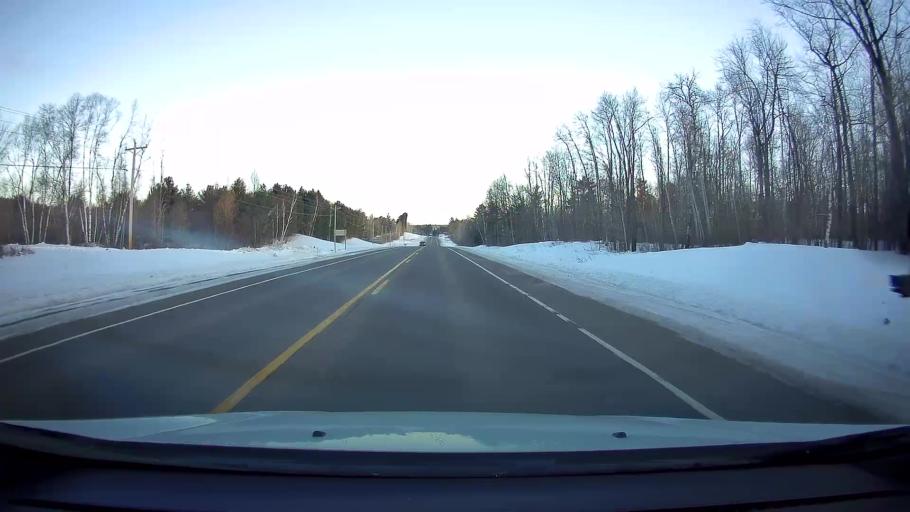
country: US
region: Wisconsin
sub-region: Barron County
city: Cumberland
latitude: 45.5901
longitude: -92.0177
